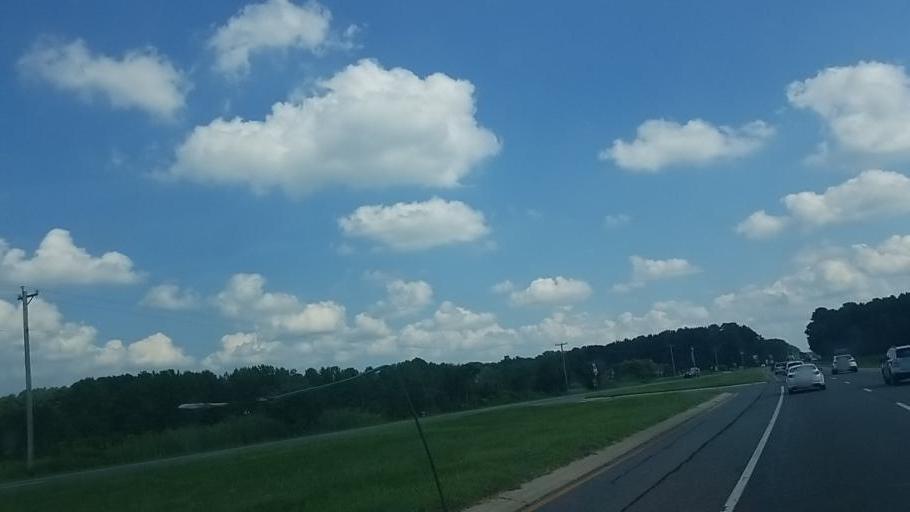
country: US
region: Delaware
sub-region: Sussex County
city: Georgetown
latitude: 38.6788
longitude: -75.3932
